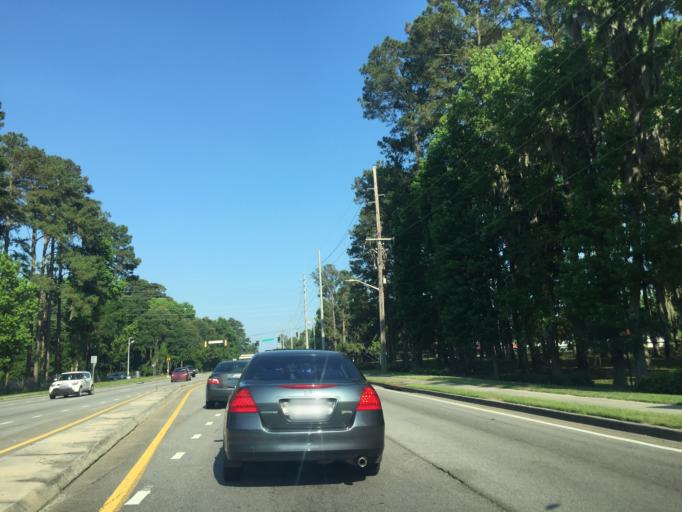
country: US
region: Georgia
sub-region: Chatham County
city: Isle of Hope
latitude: 32.0020
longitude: -81.0844
